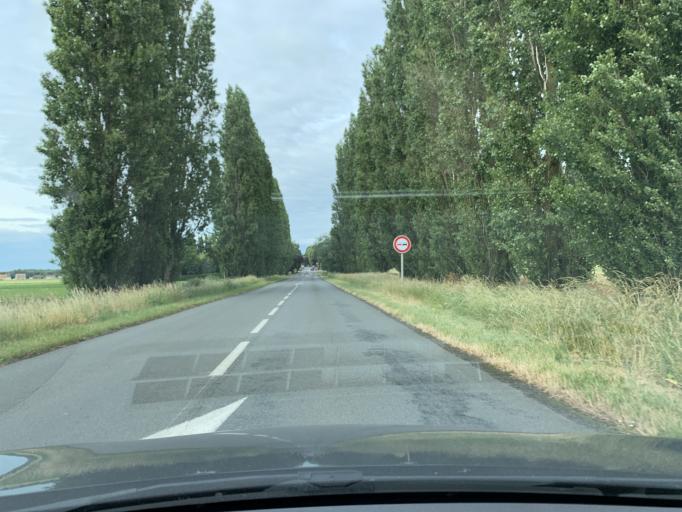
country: FR
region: Nord-Pas-de-Calais
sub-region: Departement du Nord
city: Lewarde
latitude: 50.3350
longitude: 3.1585
